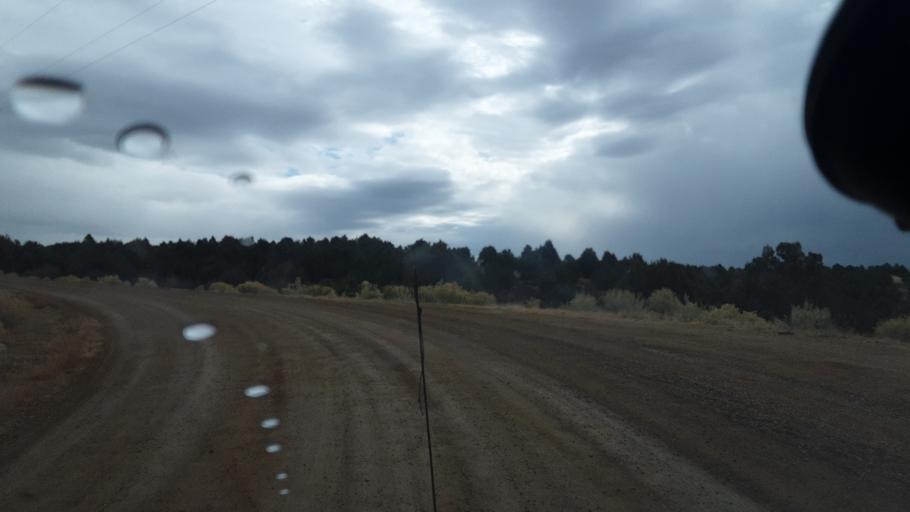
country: US
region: Colorado
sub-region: Montezuma County
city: Mancos
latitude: 37.1984
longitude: -108.1367
